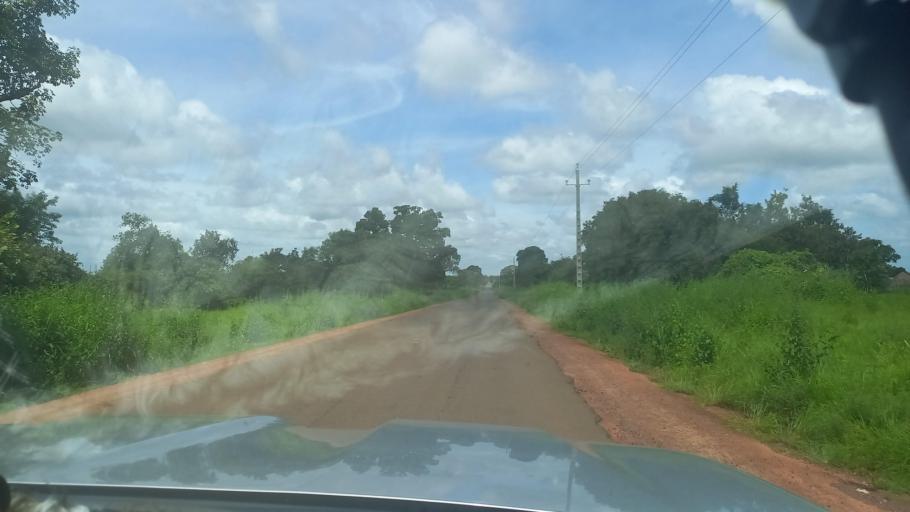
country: GM
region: Lower River
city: Kaiaf
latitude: 13.2274
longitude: -15.5380
